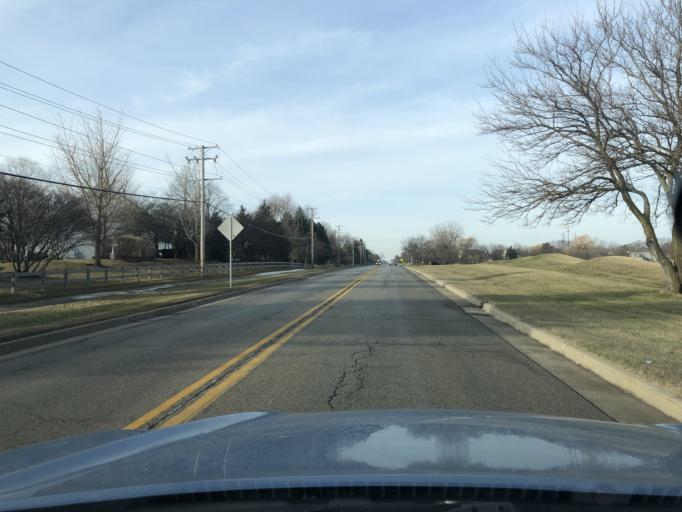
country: US
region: Illinois
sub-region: McHenry County
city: Lake in the Hills
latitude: 42.1539
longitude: -88.3220
